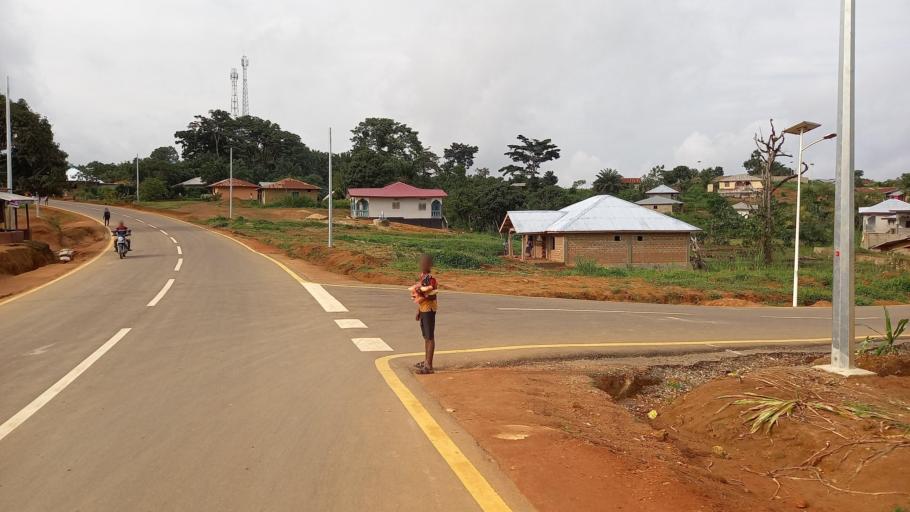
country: SL
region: Eastern Province
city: Kailahun
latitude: 8.2738
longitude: -10.5798
